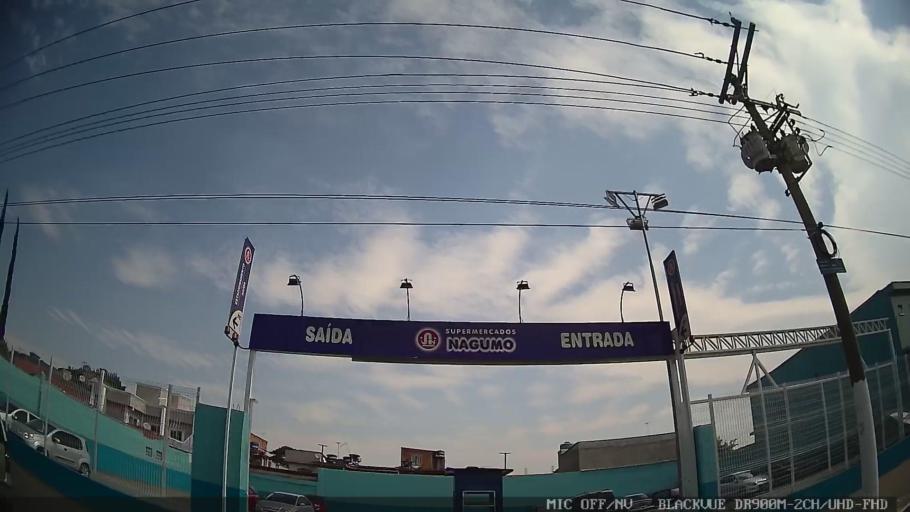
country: BR
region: Sao Paulo
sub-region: Itaquaquecetuba
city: Itaquaquecetuba
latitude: -23.4845
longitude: -46.4244
